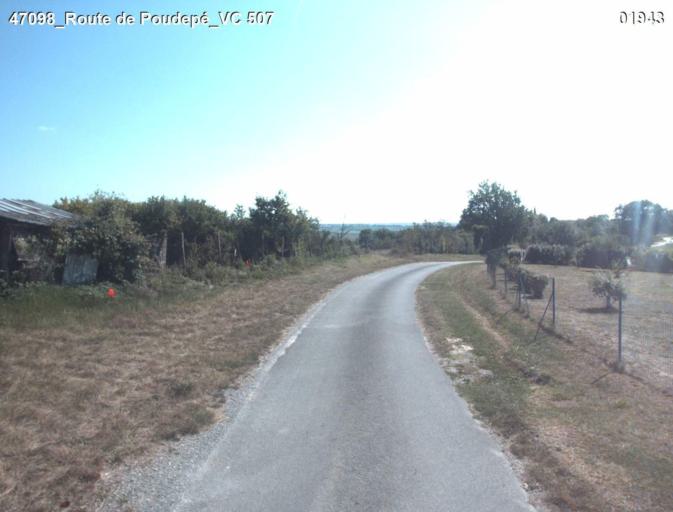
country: FR
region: Aquitaine
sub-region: Departement du Lot-et-Garonne
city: Nerac
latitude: 44.1027
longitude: 0.4018
